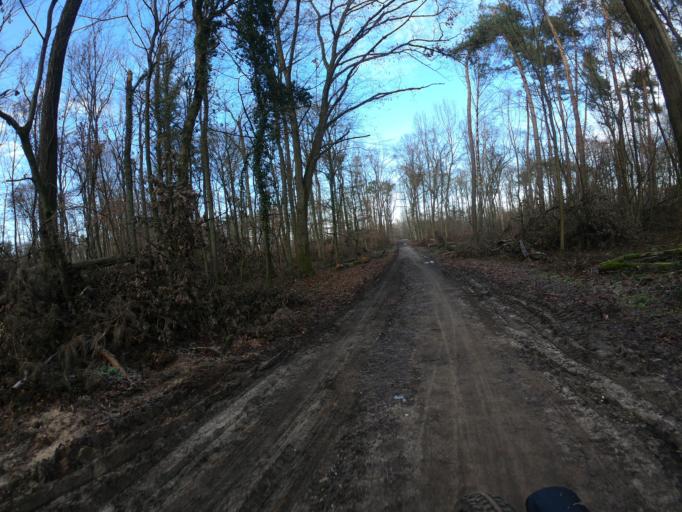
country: DE
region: Hesse
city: Morfelden-Walldorf
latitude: 49.9656
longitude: 8.5931
